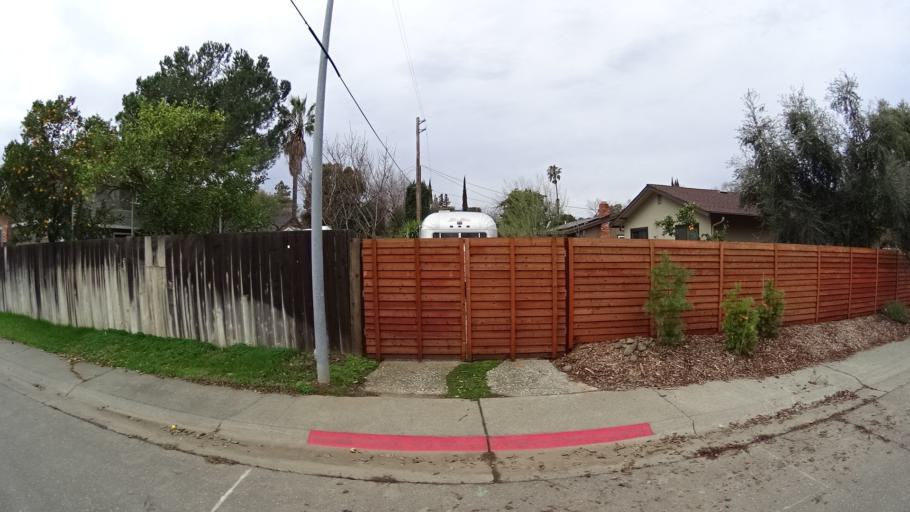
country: US
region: California
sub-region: Yolo County
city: Davis
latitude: 38.5590
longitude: -121.7205
